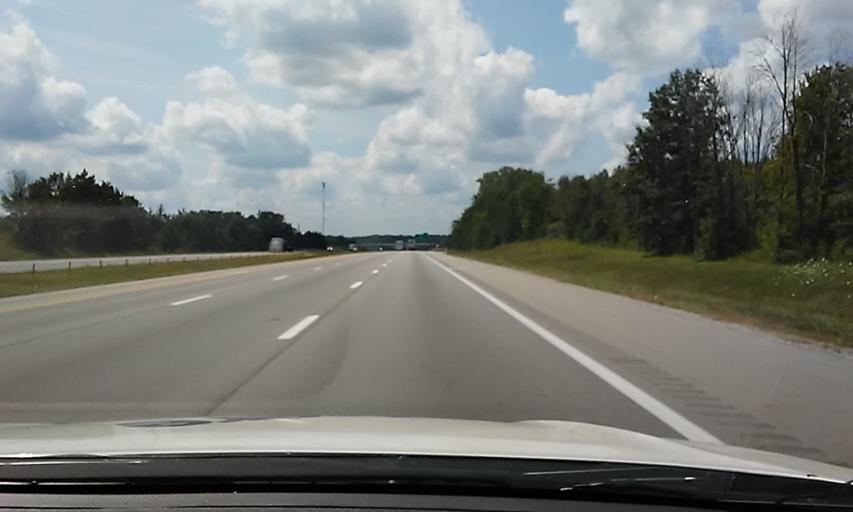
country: US
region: Ohio
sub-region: Morrow County
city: Mount Gilead
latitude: 40.5008
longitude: -82.7102
